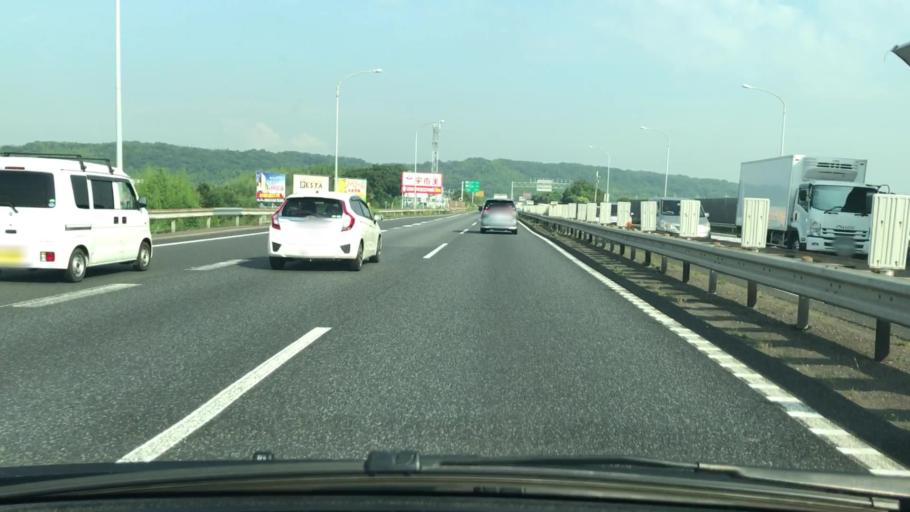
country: JP
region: Hyogo
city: Akashi
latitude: 34.6854
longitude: 134.9791
